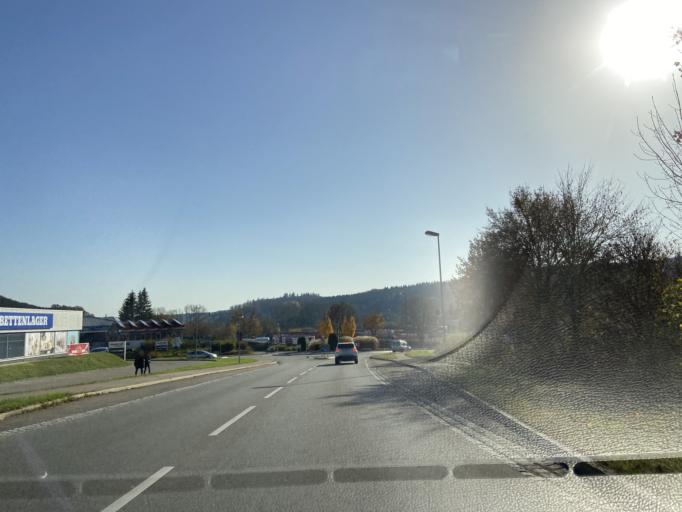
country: DE
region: Baden-Wuerttemberg
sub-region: Tuebingen Region
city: Sigmaringen
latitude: 48.0814
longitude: 9.2320
